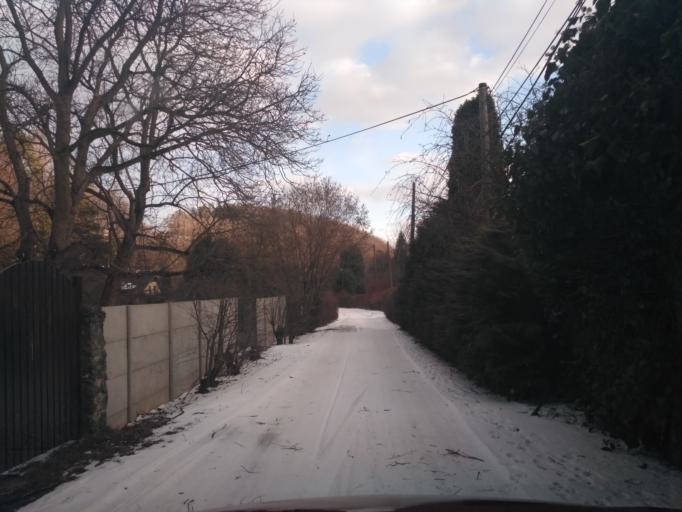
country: SK
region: Kosicky
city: Kosice
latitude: 48.7305
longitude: 21.1614
